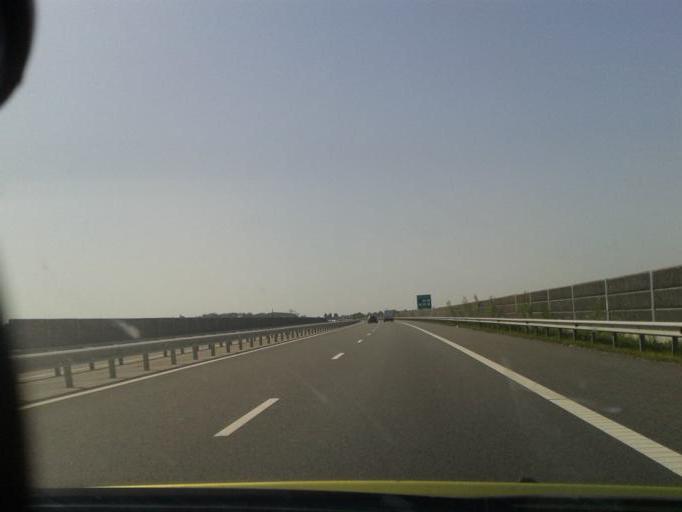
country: RO
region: Prahova
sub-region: Comuna Rafov
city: Rafov
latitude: 44.8756
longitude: 26.1378
